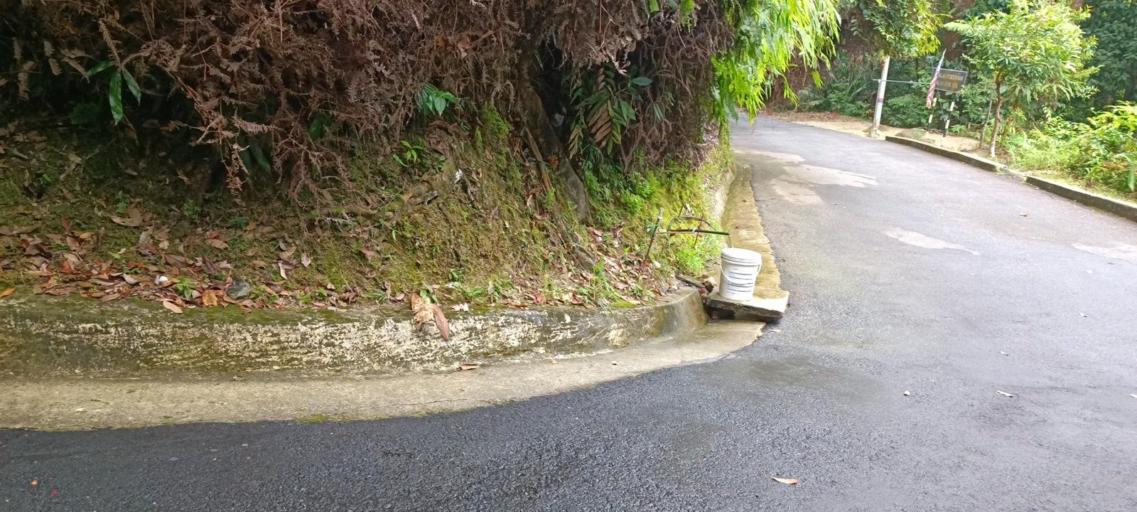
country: MY
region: Perak
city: Taiping
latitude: 4.8624
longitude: 100.7659
